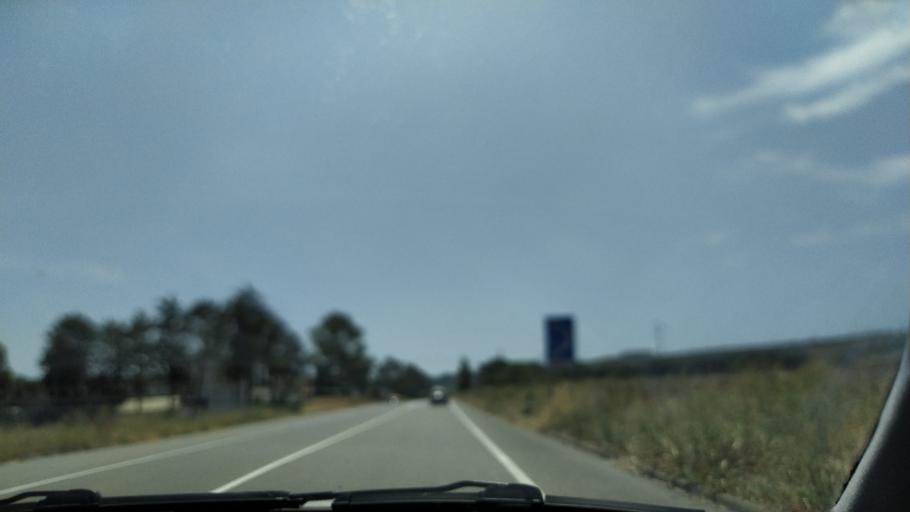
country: IT
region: Basilicate
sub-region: Provincia di Matera
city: Bernalda
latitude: 40.4456
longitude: 16.7790
